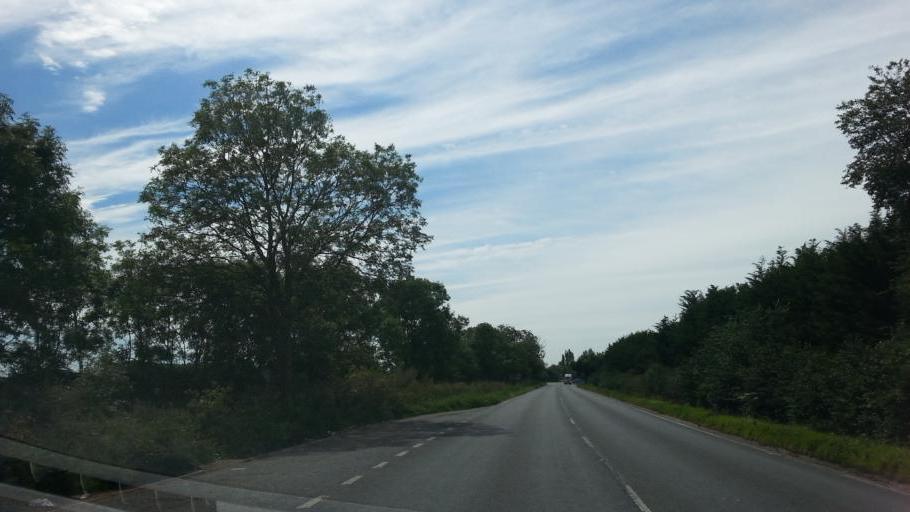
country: GB
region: England
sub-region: Cambridgeshire
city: Waterbeach
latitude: 52.2935
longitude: 0.1799
